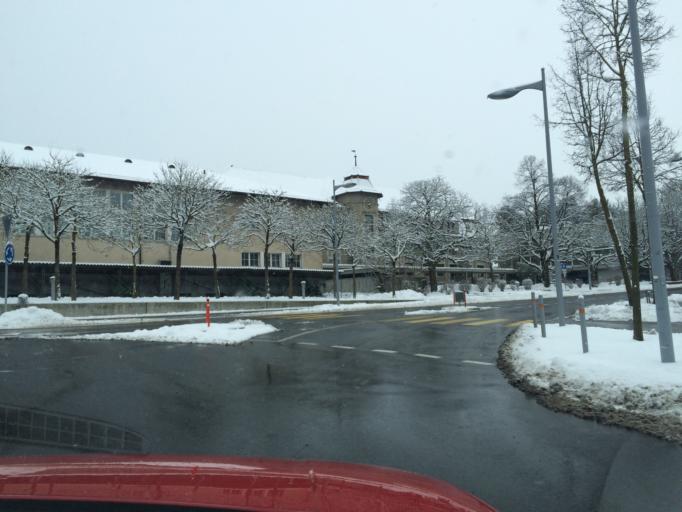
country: CH
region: Bern
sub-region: Bern-Mittelland District
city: Koniz
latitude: 46.9204
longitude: 7.4132
